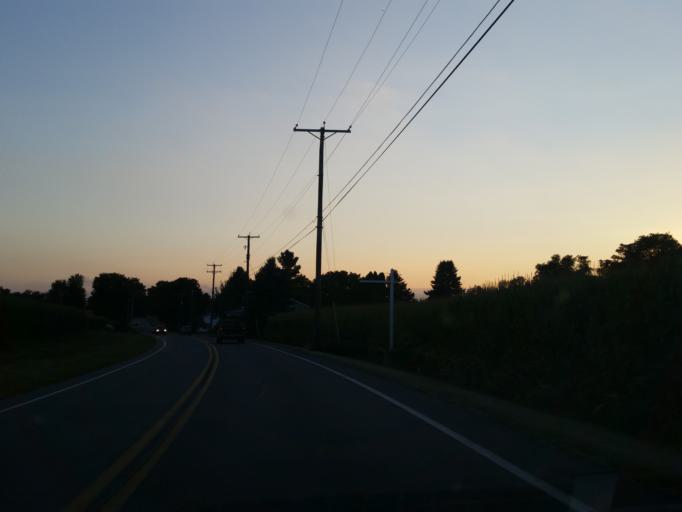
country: US
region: Pennsylvania
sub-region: Lebanon County
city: Cornwall
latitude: 40.2856
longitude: -76.3975
